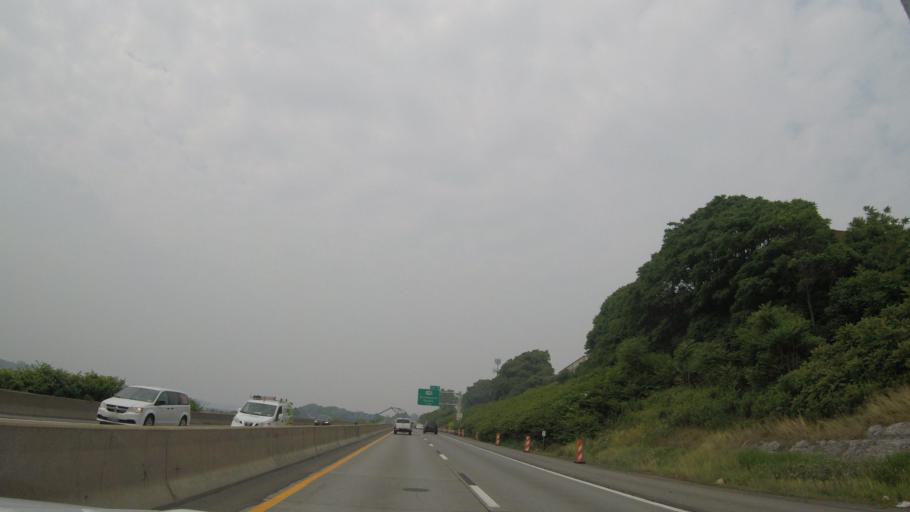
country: US
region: New York
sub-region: Erie County
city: Buffalo
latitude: 42.9094
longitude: -78.9014
